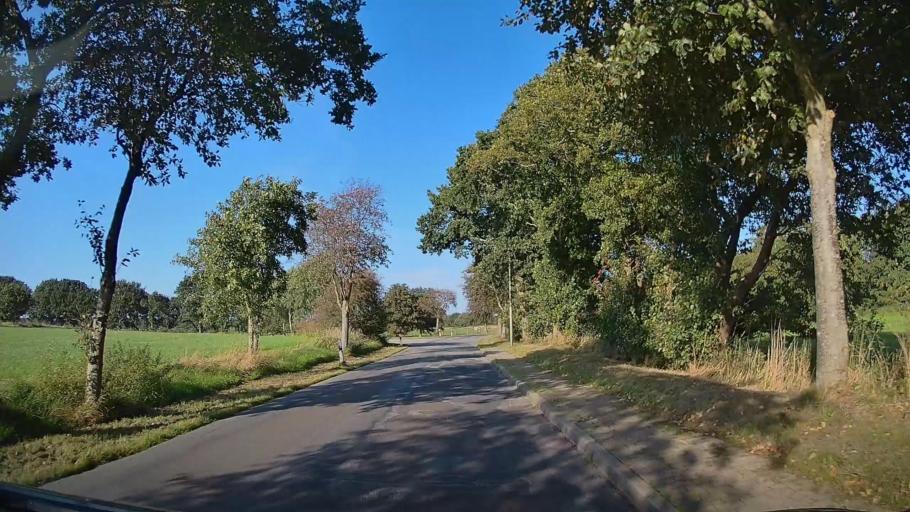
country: DE
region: Lower Saxony
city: Cuxhaven
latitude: 53.8502
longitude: 8.6567
